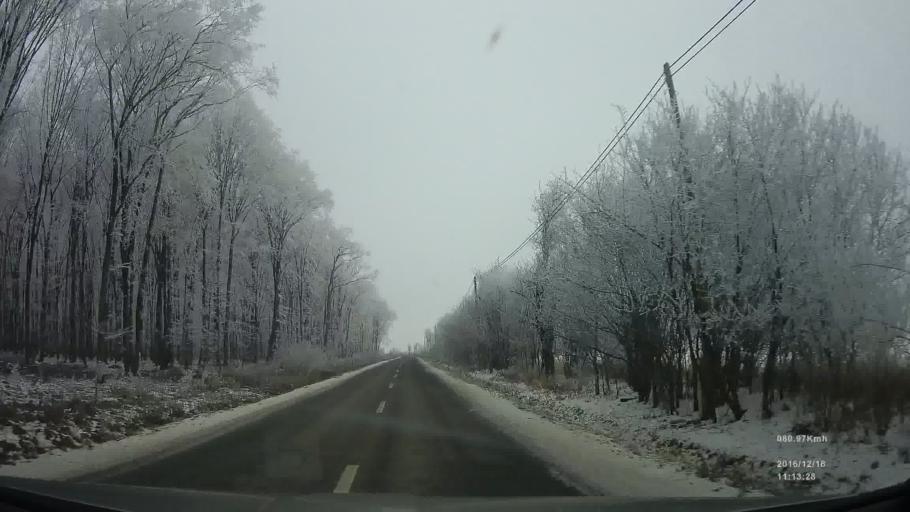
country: SK
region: Presovsky
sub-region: Okres Presov
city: Presov
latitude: 48.8826
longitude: 21.3126
